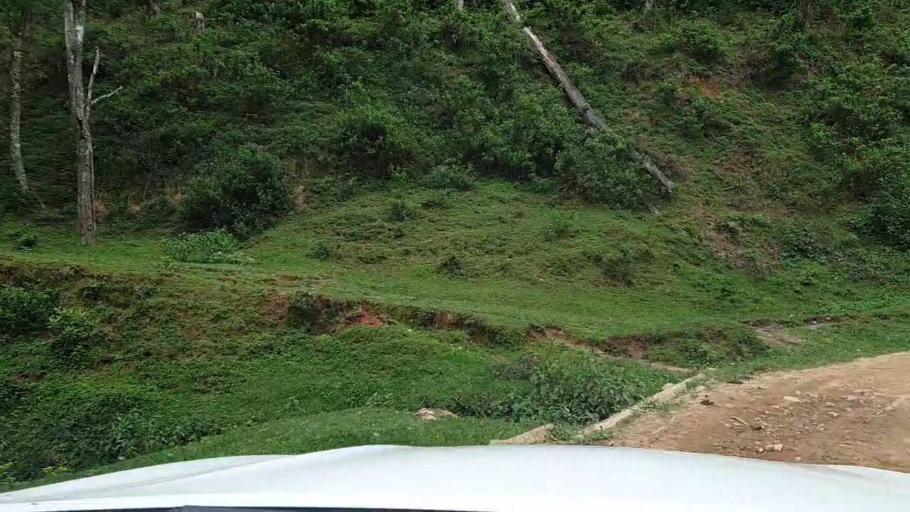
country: RW
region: Western Province
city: Kibuye
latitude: -2.2918
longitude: 29.3705
